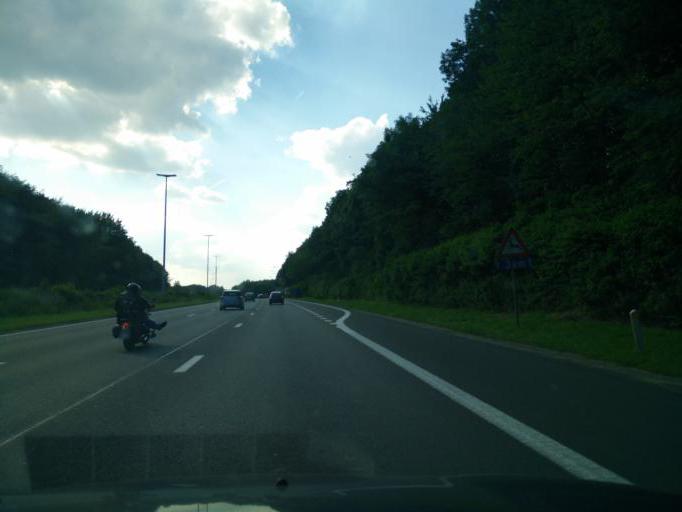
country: BE
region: Wallonia
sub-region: Province du Brabant Wallon
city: Braine-le-Chateau
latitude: 50.6952
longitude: 4.2920
